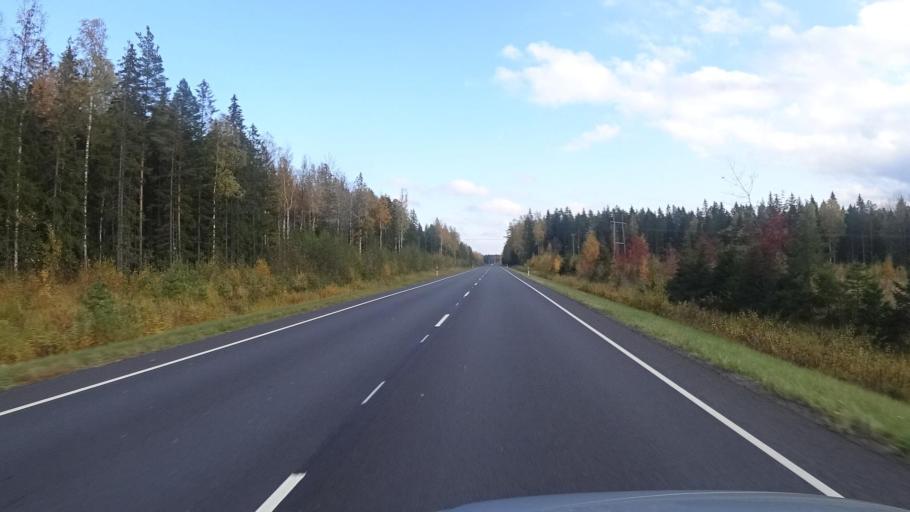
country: FI
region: Satakunta
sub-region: Rauma
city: Eura
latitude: 61.1140
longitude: 22.1984
